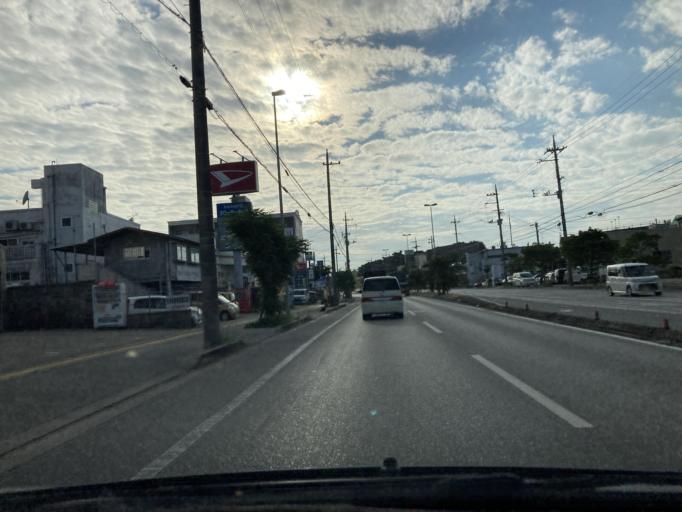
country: JP
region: Okinawa
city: Okinawa
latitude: 26.3587
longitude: 127.8080
